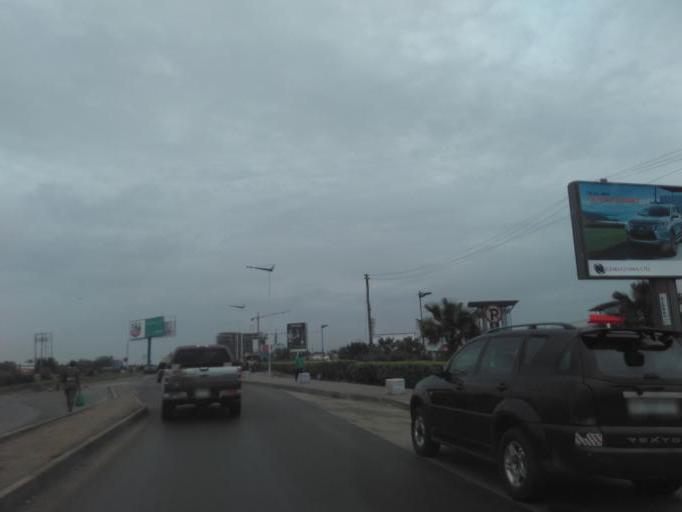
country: GH
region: Greater Accra
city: Medina Estates
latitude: 5.6221
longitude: -0.1746
